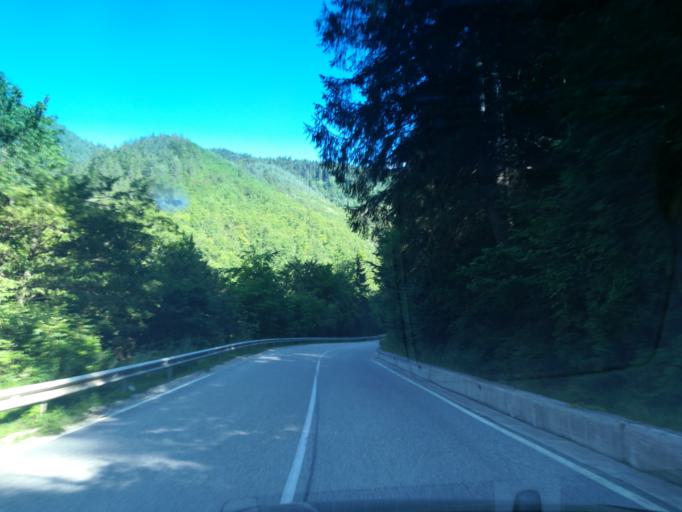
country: BG
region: Smolyan
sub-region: Obshtina Chepelare
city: Chepelare
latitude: 41.7758
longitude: 24.7071
